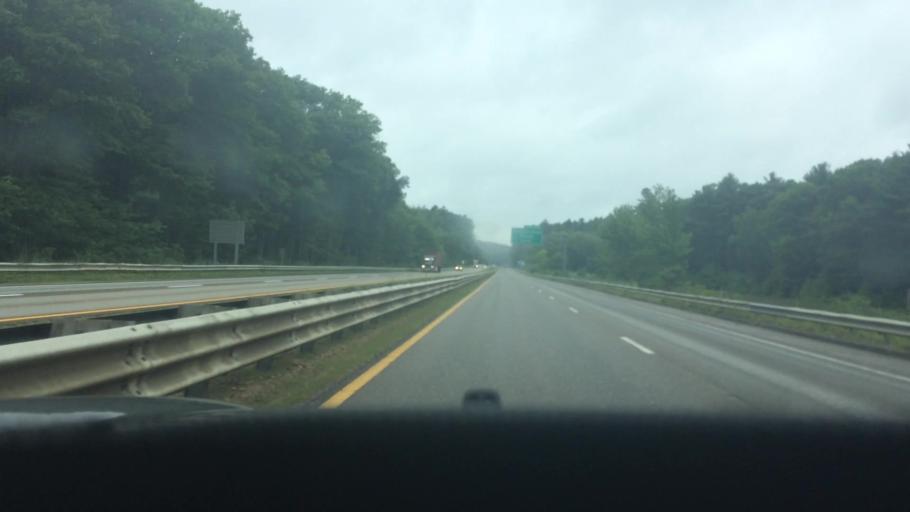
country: US
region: Massachusetts
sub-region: Worcester County
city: Harvard
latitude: 42.5182
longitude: -71.6159
